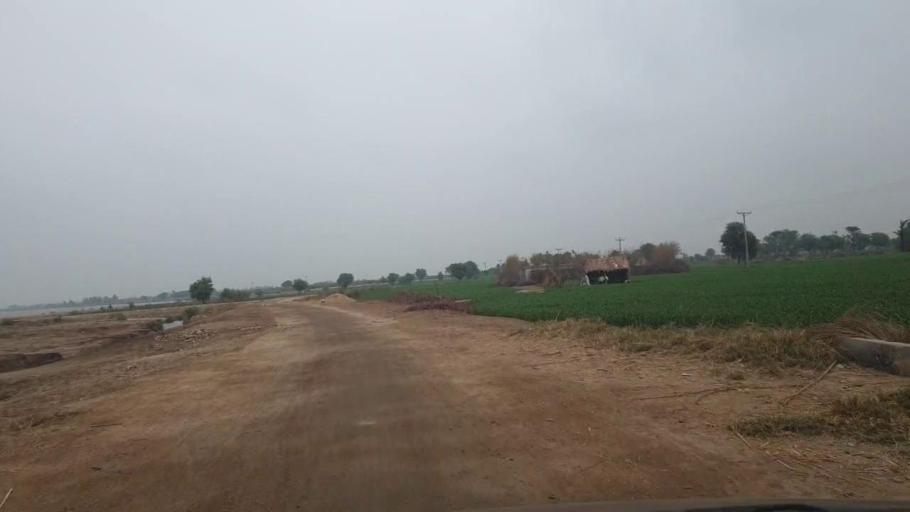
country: PK
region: Sindh
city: Tando Adam
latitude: 25.8545
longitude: 68.7029
